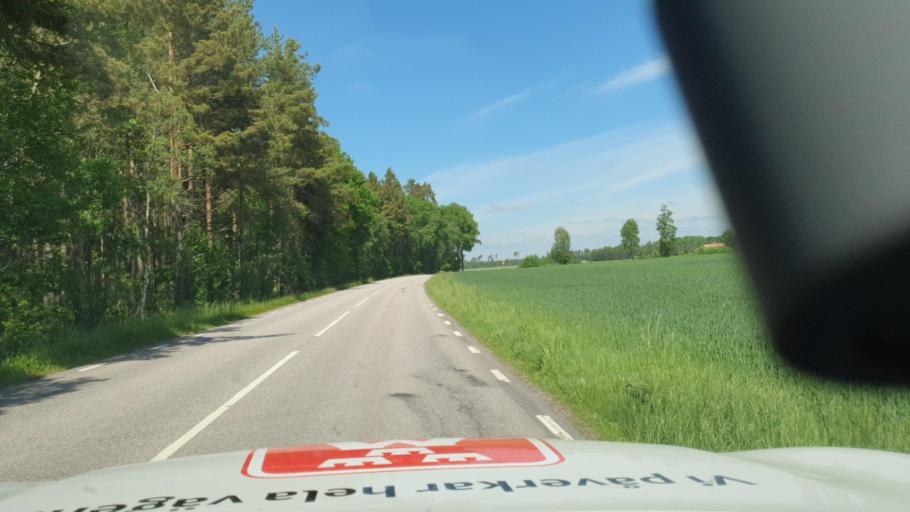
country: SE
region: Vaestra Goetaland
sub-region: Vara Kommun
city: Vara
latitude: 58.2200
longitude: 13.0017
